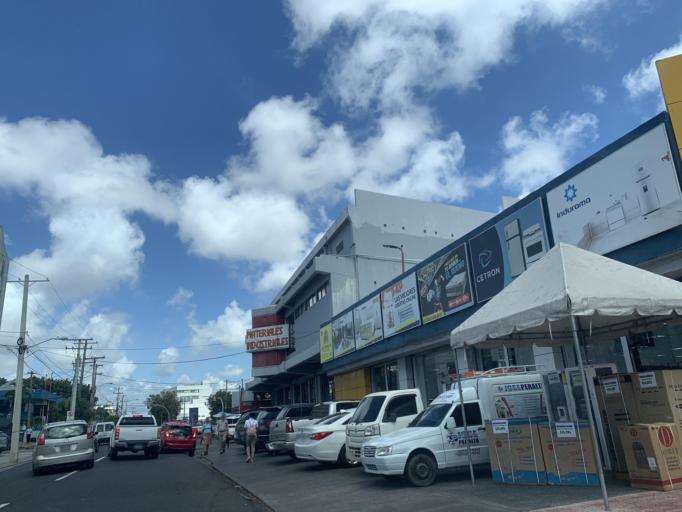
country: DO
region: Nacional
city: San Carlos
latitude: 18.4844
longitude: -69.9133
